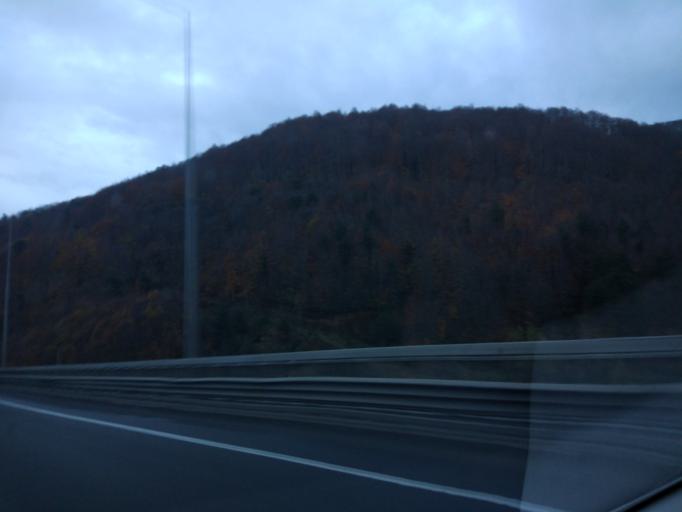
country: TR
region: Duzce
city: Kaynasli
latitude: 40.7610
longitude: 31.4116
